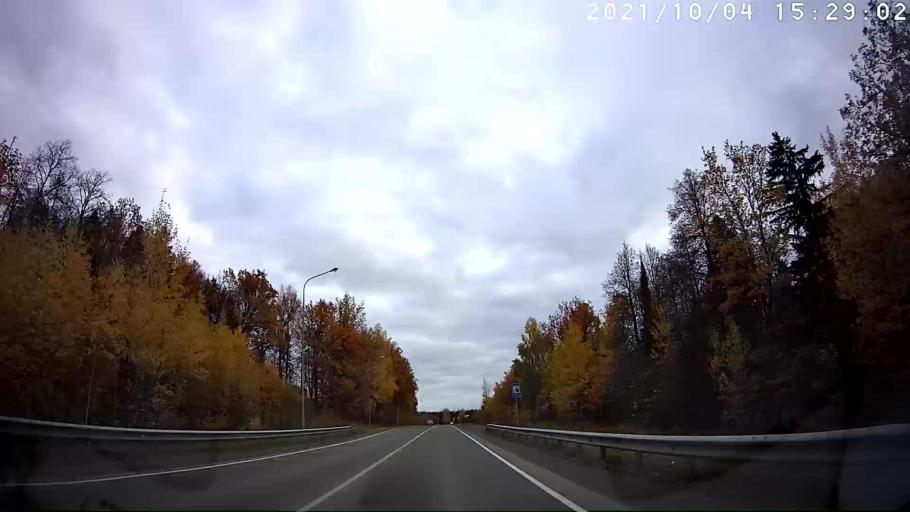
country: RU
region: Mariy-El
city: Yoshkar-Ola
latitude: 56.6037
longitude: 47.9712
